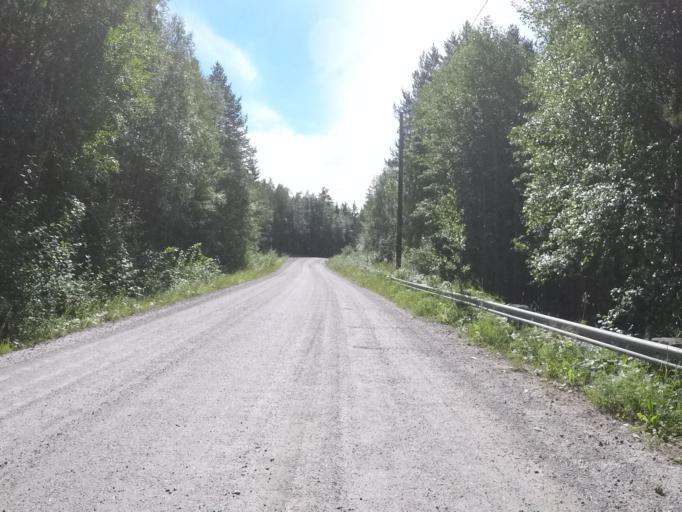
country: SE
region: Vaesterbotten
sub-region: Robertsfors Kommun
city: Robertsfors
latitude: 64.0060
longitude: 20.8138
